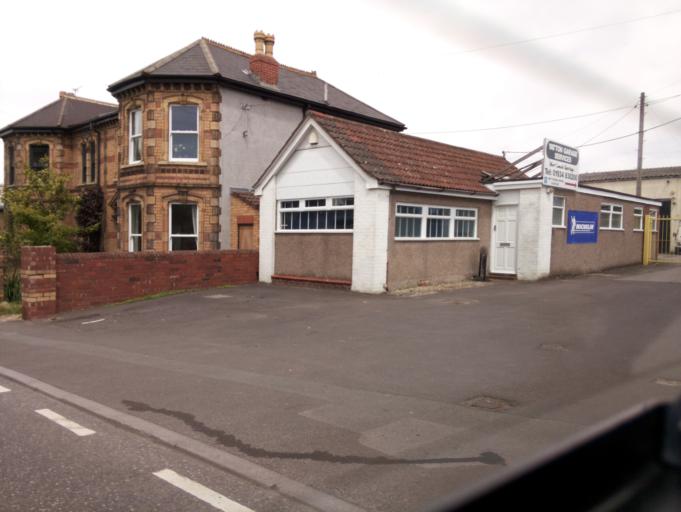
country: GB
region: England
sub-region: North Somerset
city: Yatton
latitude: 51.3918
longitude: -2.8262
